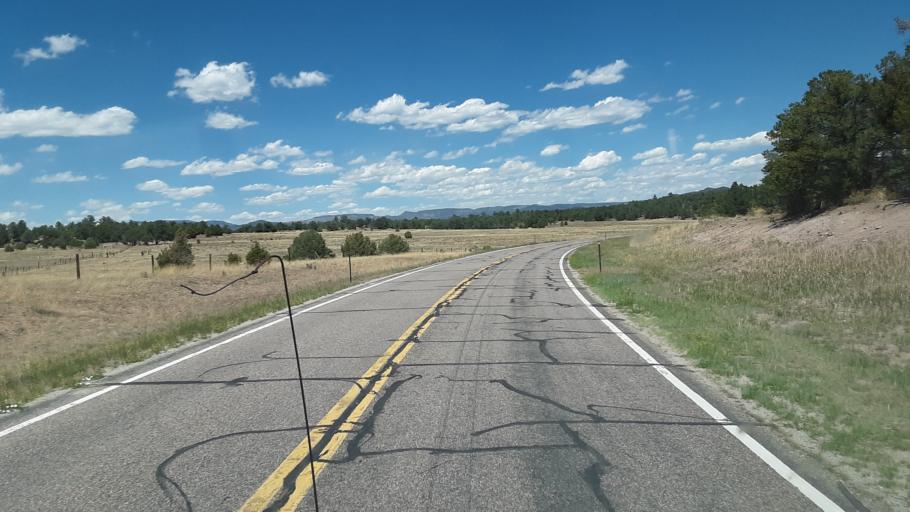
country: US
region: Colorado
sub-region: Custer County
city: Westcliffe
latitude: 38.3142
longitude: -105.6197
